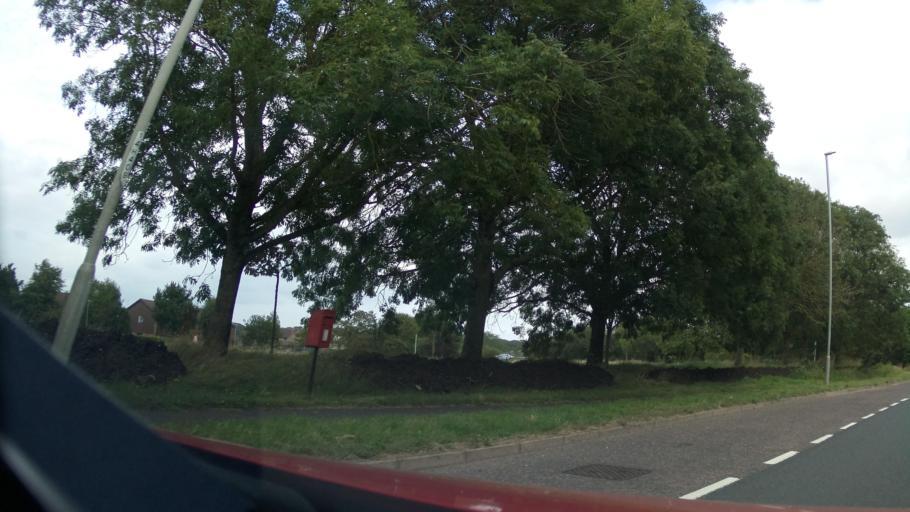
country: GB
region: England
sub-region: Hampshire
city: Bransgore
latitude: 50.7421
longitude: -1.7376
